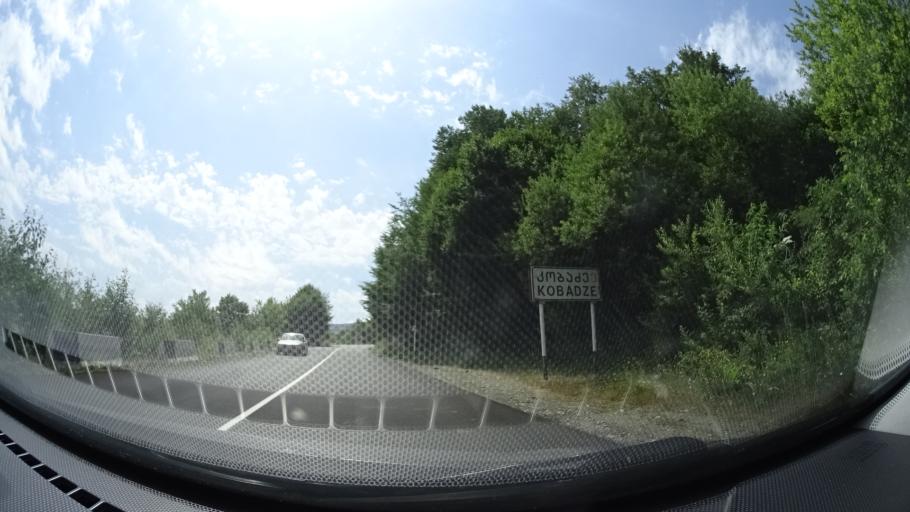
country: GE
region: Kakheti
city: Sagarejo
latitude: 41.8617
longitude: 45.3182
